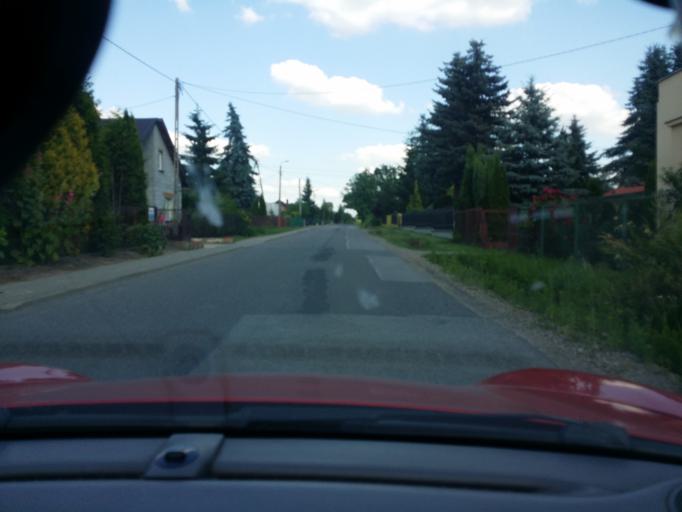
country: PL
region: Masovian Voivodeship
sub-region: Powiat radomski
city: Trablice
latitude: 51.3508
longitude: 21.1435
